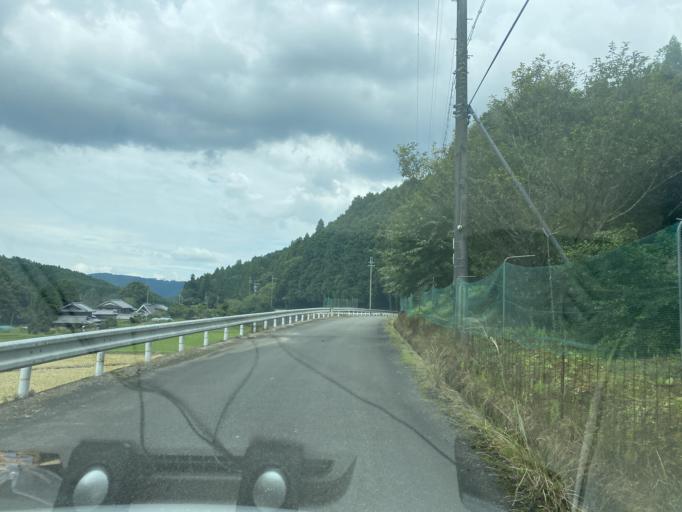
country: JP
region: Nara
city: Nara-shi
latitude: 34.6779
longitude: 135.8956
